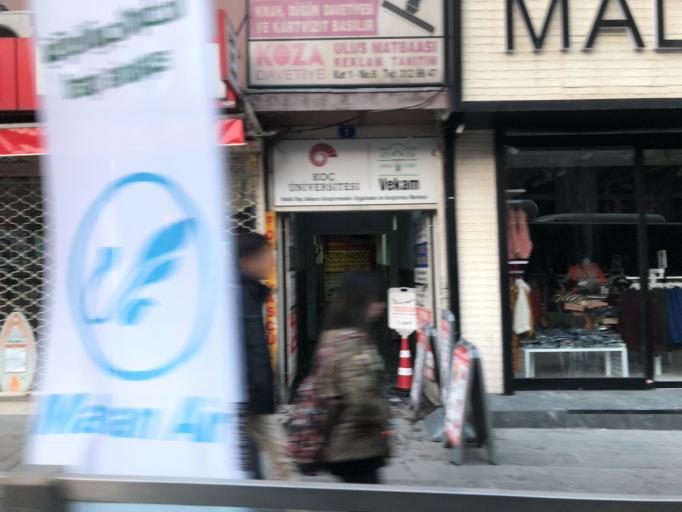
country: TR
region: Ankara
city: Ankara
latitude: 39.9428
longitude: 32.8544
